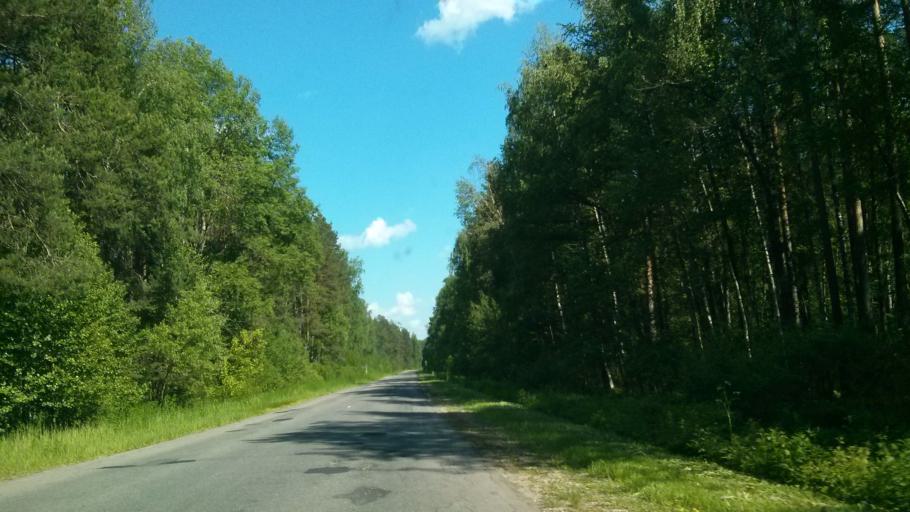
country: RU
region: Vladimir
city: Melenki
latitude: 55.3334
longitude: 41.6776
